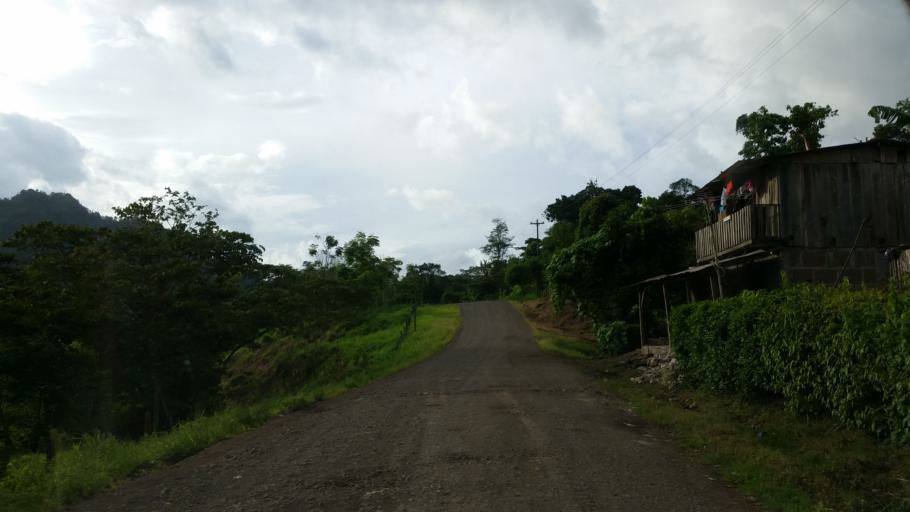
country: NI
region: Jinotega
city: Jinotega
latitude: 13.2562
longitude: -85.7373
